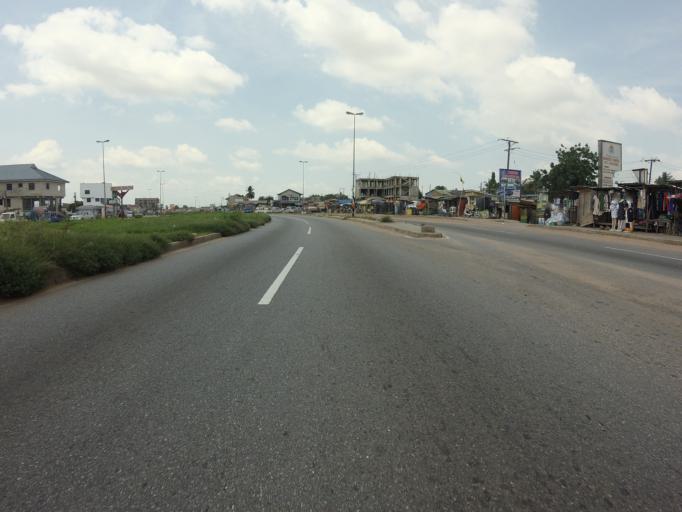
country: GH
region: Greater Accra
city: Gbawe
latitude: 5.6268
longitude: -0.3087
